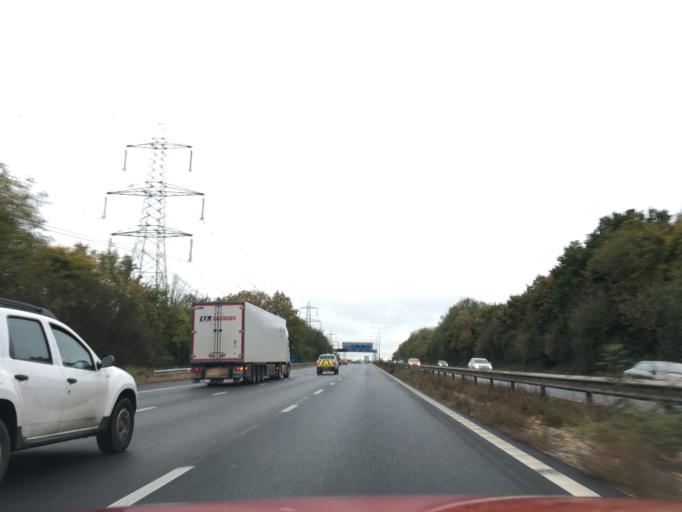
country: GB
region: England
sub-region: Hampshire
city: Eastleigh
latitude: 50.9796
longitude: -1.3689
